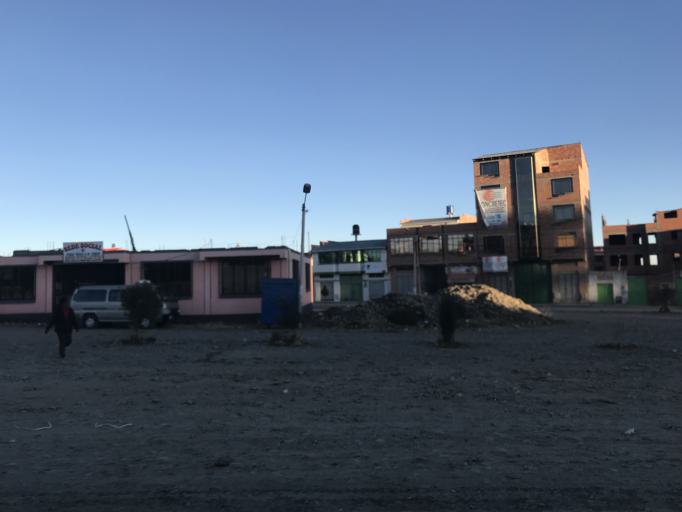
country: BO
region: La Paz
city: La Paz
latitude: -16.4985
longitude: -68.2310
